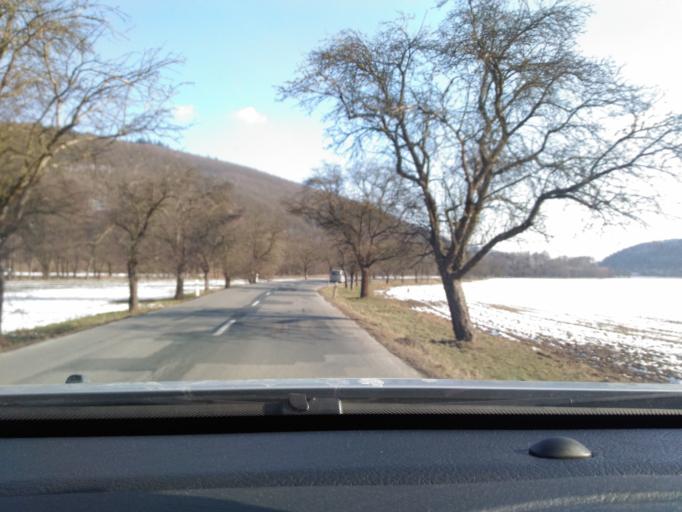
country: CZ
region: South Moravian
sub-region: Okres Brno-Venkov
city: Dolni Loucky
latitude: 49.3909
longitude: 16.3717
